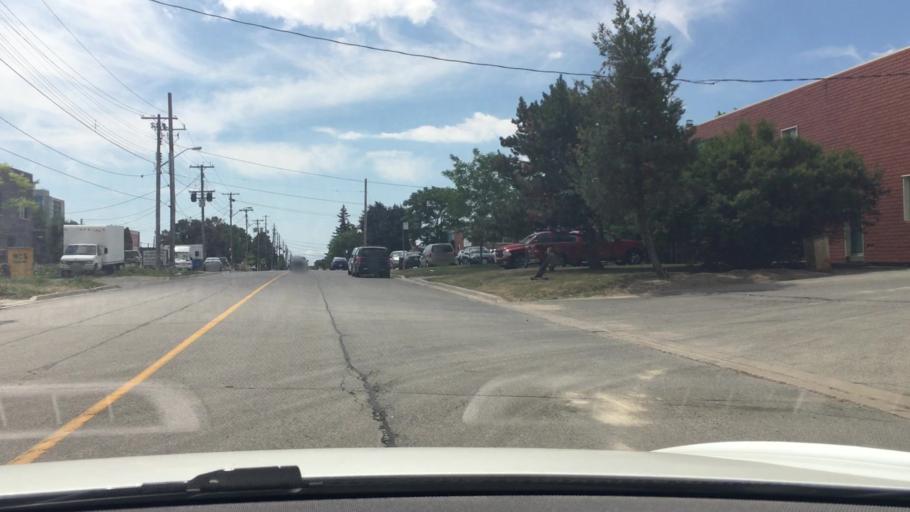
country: CA
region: Ontario
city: Scarborough
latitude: 43.7526
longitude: -79.2904
